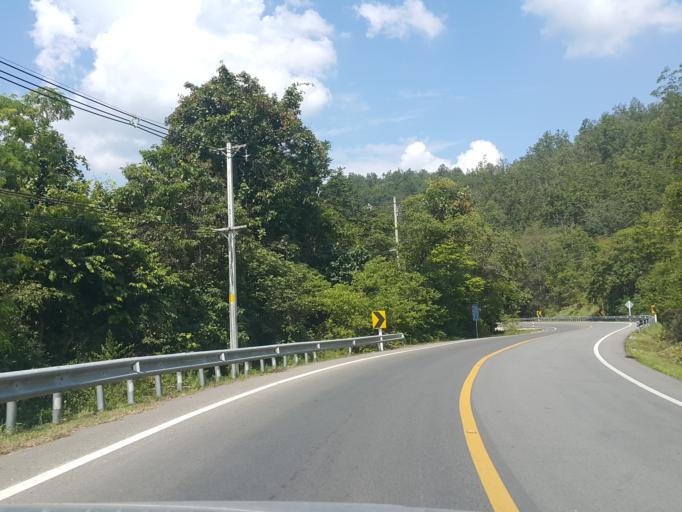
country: TH
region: Chiang Mai
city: Chom Thong
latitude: 18.5025
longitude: 98.6659
